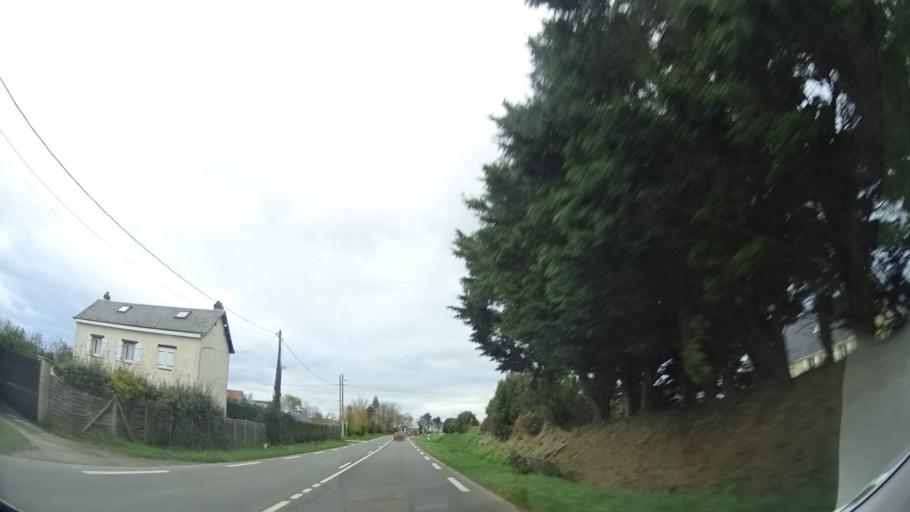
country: FR
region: Haute-Normandie
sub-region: Departement de la Seine-Maritime
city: Cauville-sur-Mer
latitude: 49.5878
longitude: 0.1265
